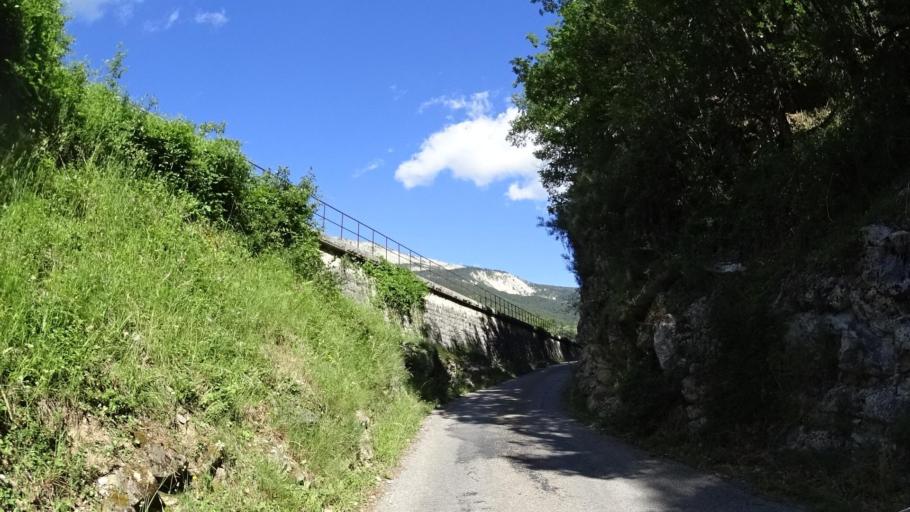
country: FR
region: Provence-Alpes-Cote d'Azur
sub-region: Departement des Alpes-de-Haute-Provence
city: Annot
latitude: 44.0109
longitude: 6.6378
